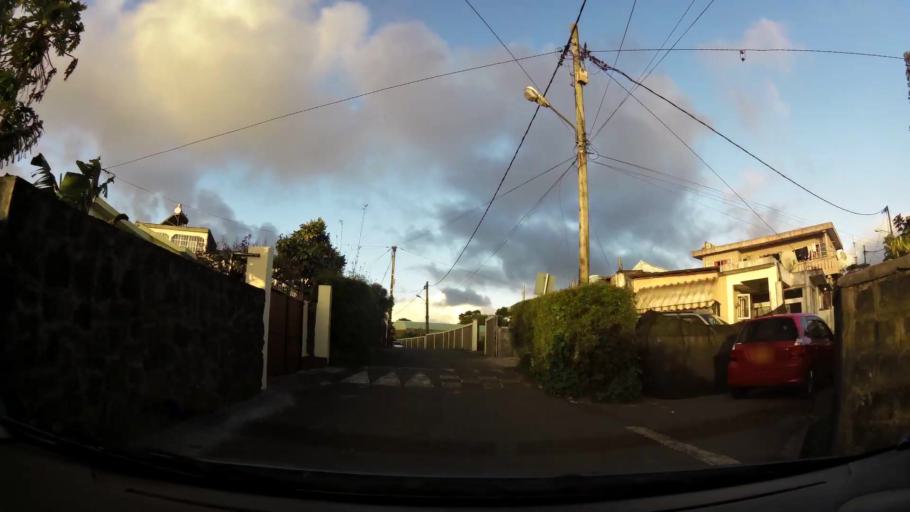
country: MU
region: Plaines Wilhems
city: Curepipe
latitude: -20.3080
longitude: 57.5314
